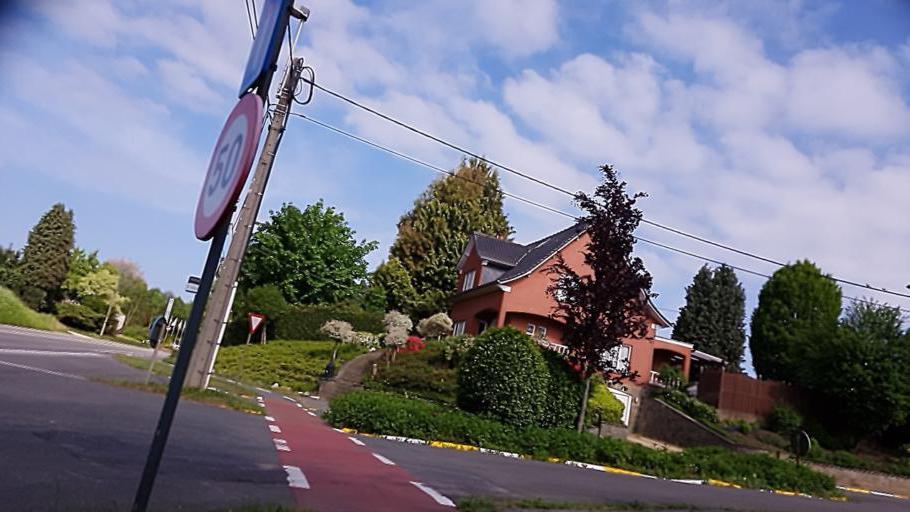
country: BE
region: Flanders
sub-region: Provincie Vlaams-Brabant
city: Overijse
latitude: 50.7593
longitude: 4.5636
